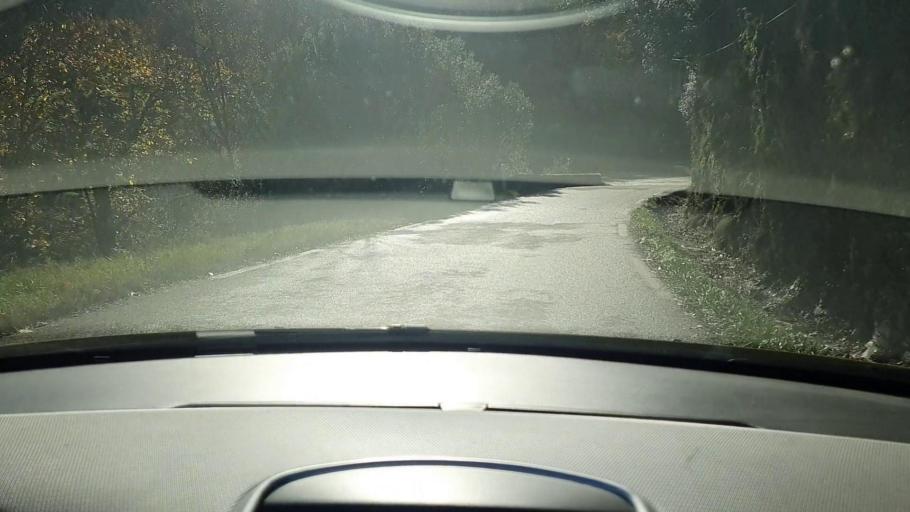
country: FR
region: Languedoc-Roussillon
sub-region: Departement du Gard
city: Valleraugue
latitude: 44.1597
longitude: 3.6527
